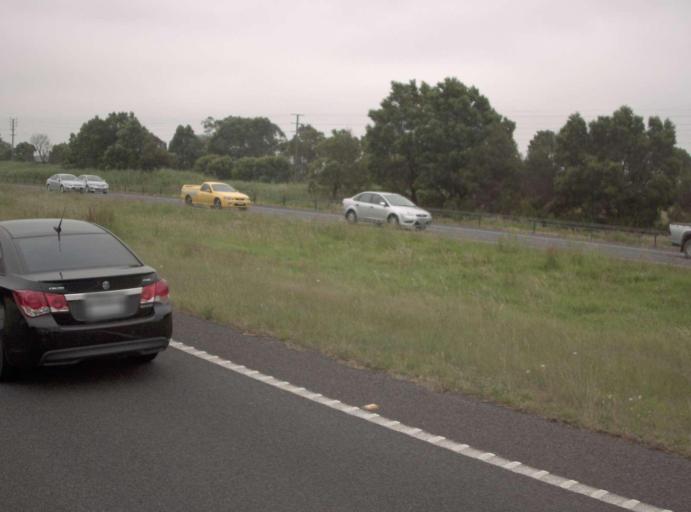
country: AU
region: Victoria
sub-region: Baw Baw
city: Warragul
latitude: -38.2058
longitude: 146.0889
